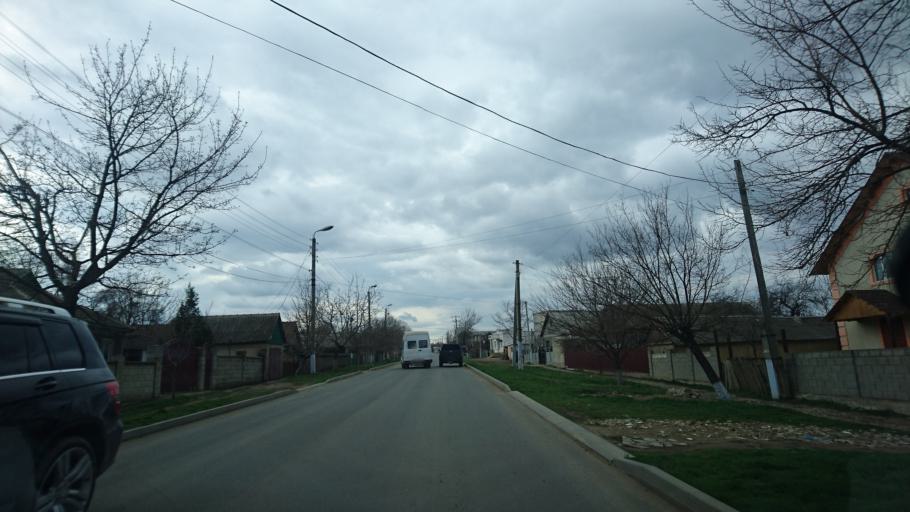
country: MD
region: Gagauzia
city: Comrat
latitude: 46.3028
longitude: 28.6416
